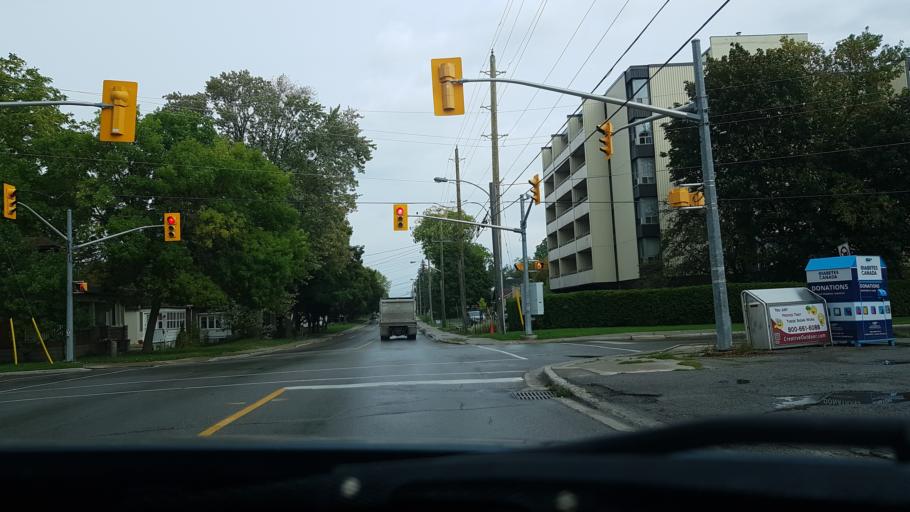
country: CA
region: Ontario
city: Omemee
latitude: 44.3580
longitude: -78.7509
